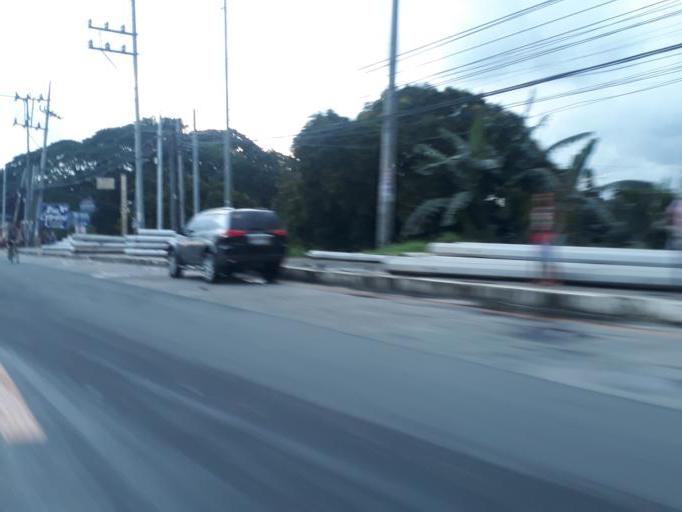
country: PH
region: Metro Manila
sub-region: Quezon City
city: Quezon City
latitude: 14.6724
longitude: 121.0788
